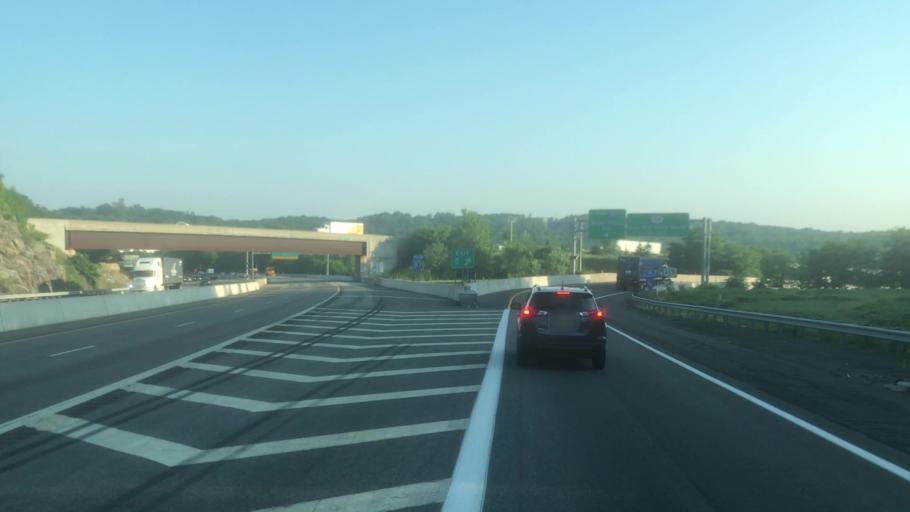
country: US
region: New York
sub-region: Westchester County
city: Elmsford
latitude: 41.0554
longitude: -73.8343
